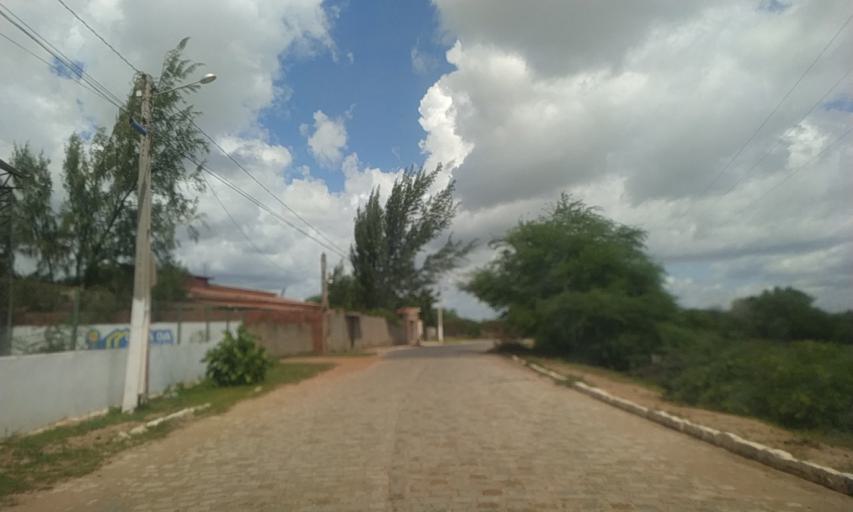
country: BR
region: Rio Grande do Norte
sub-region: Areia Branca
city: Areia Branca
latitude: -4.9332
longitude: -37.1105
